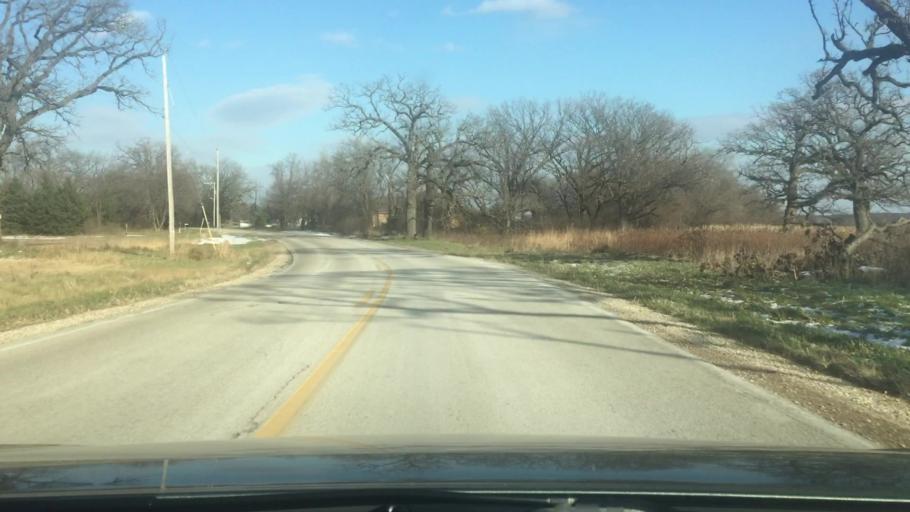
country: US
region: Wisconsin
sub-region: Waukesha County
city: Eagle
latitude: 42.9189
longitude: -88.5143
